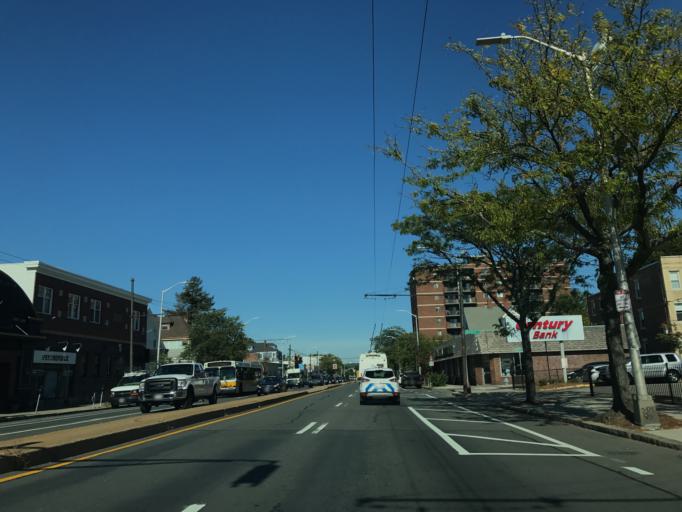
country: US
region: Massachusetts
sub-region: Middlesex County
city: Somerville
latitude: 42.3954
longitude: -71.1278
